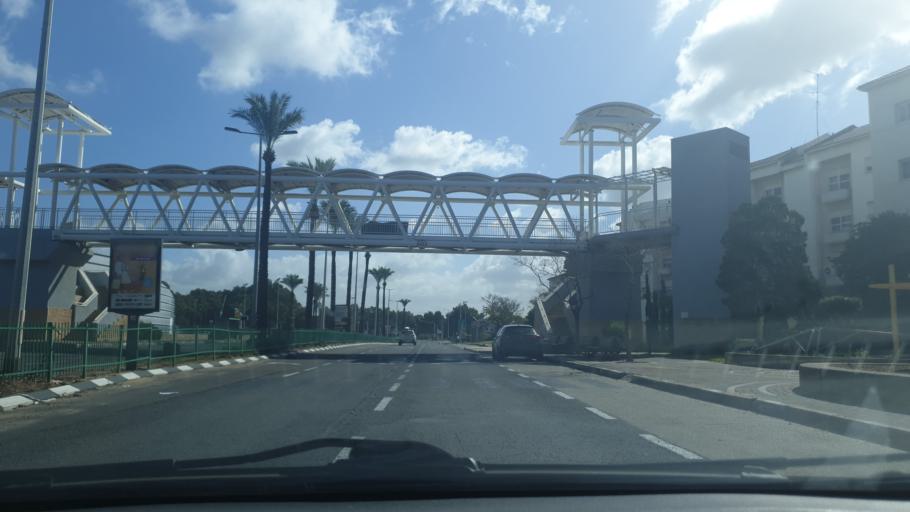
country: IL
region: Haifa
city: Qesarya
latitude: 32.5014
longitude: 34.9257
